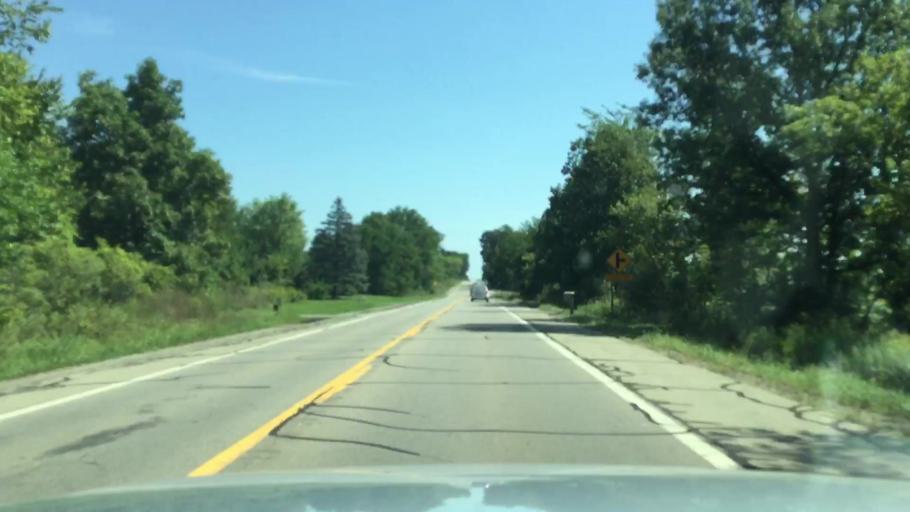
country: US
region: Michigan
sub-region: Washtenaw County
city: Manchester
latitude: 42.0729
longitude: -84.0501
